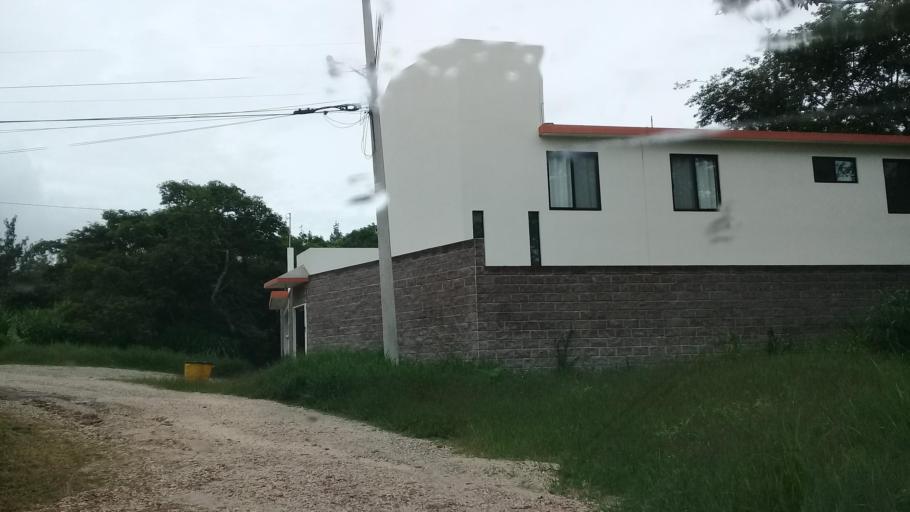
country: MX
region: Veracruz
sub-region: Emiliano Zapata
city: Jacarandas
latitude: 19.5029
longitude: -96.8404
